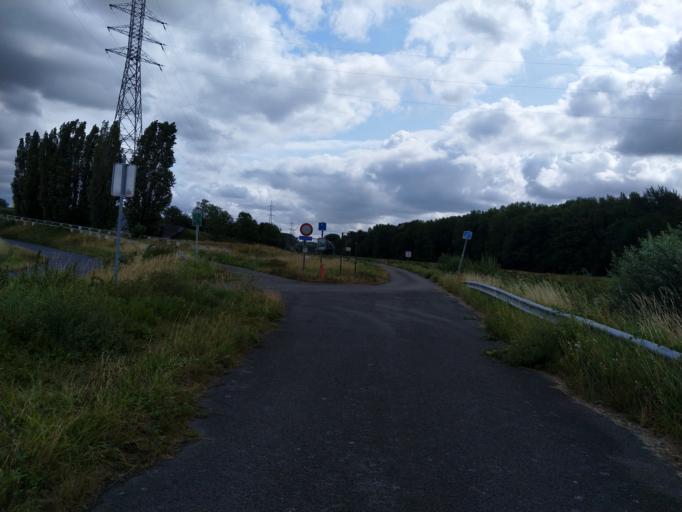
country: BE
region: Wallonia
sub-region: Province du Hainaut
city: Saint-Ghislain
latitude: 50.4737
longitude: 3.8296
